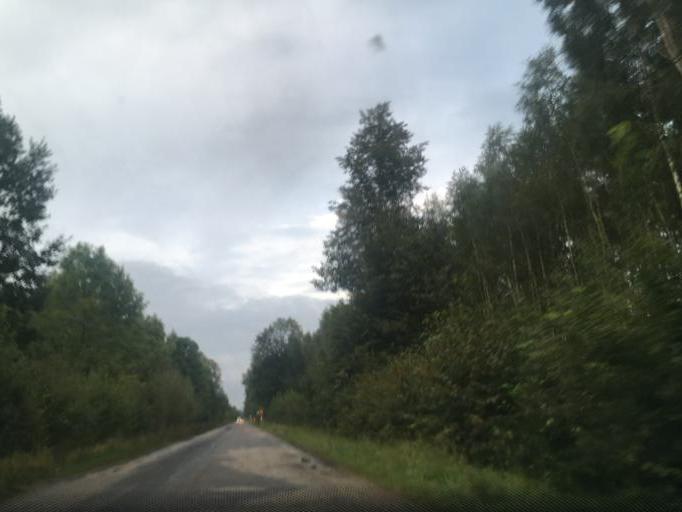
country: PL
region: Podlasie
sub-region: Powiat hajnowski
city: Hajnowka
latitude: 52.8230
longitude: 23.6962
